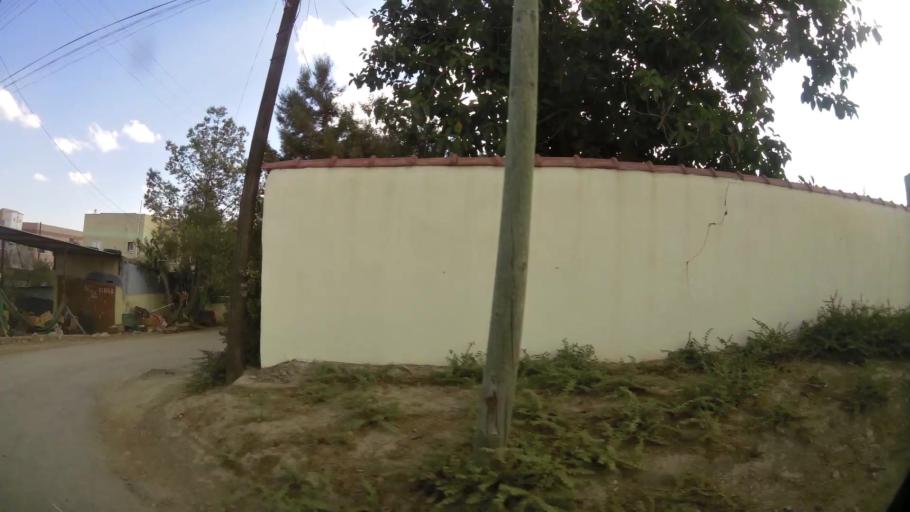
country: CY
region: Lefkosia
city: Nicosia
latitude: 35.2268
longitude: 33.3788
